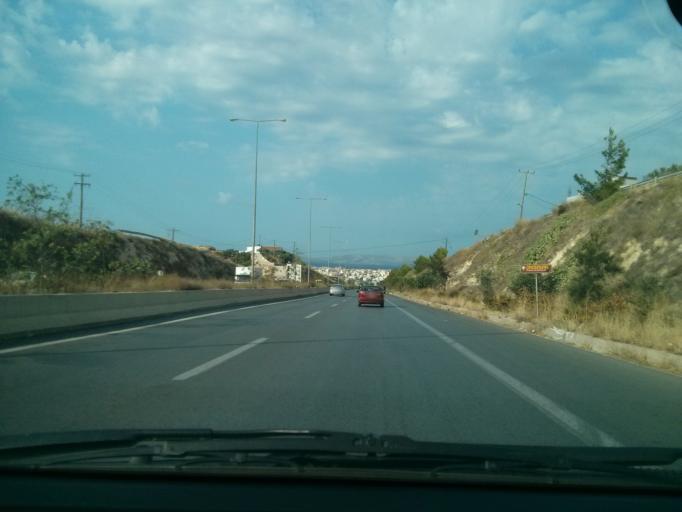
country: GR
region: Crete
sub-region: Nomos Irakleiou
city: Irakleion
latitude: 35.3245
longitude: 25.1505
